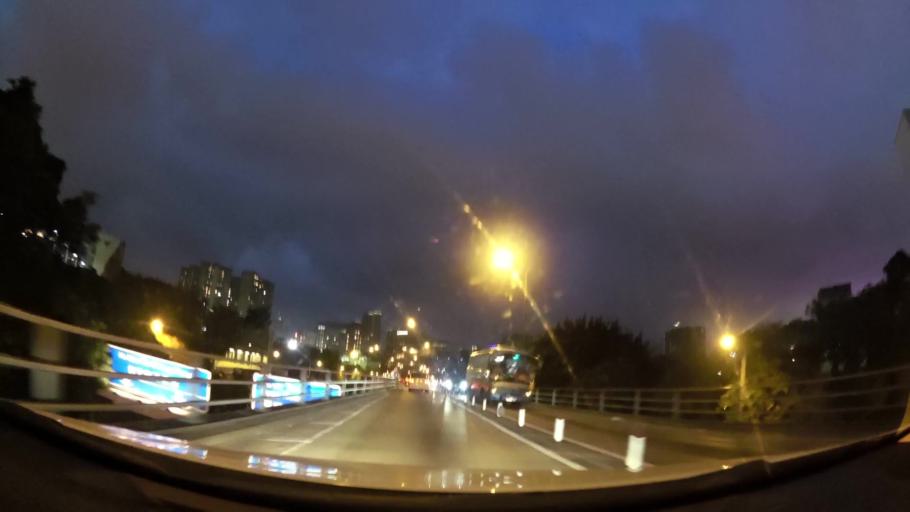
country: HK
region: Kowloon City
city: Kowloon
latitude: 22.3070
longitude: 114.1745
